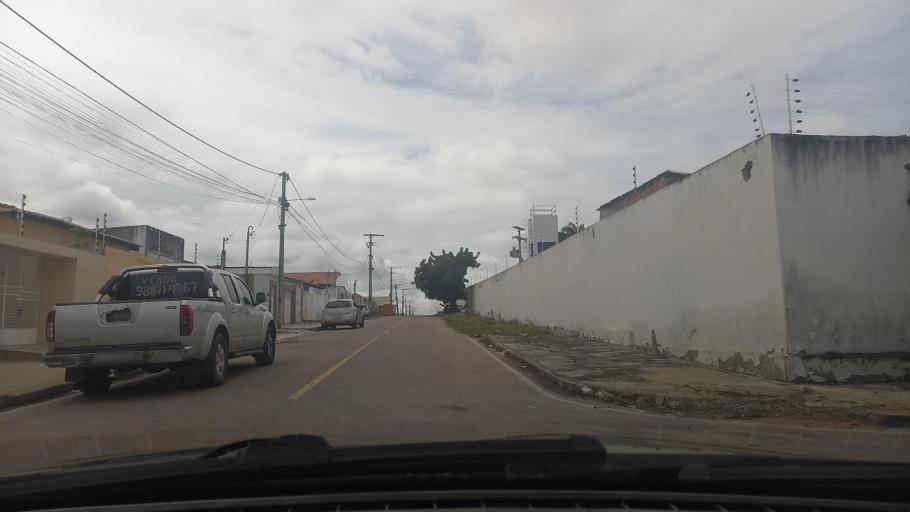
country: BR
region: Bahia
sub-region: Paulo Afonso
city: Paulo Afonso
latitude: -9.4017
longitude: -38.2434
